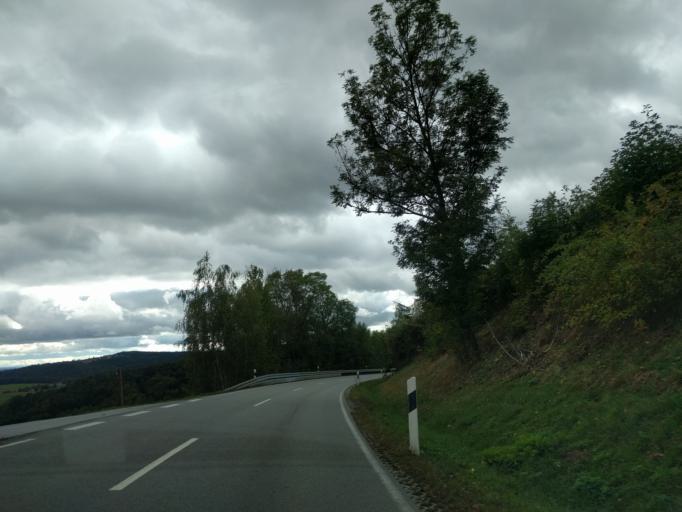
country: DE
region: Bavaria
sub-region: Lower Bavaria
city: Schaufling
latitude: 48.8571
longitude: 13.0720
